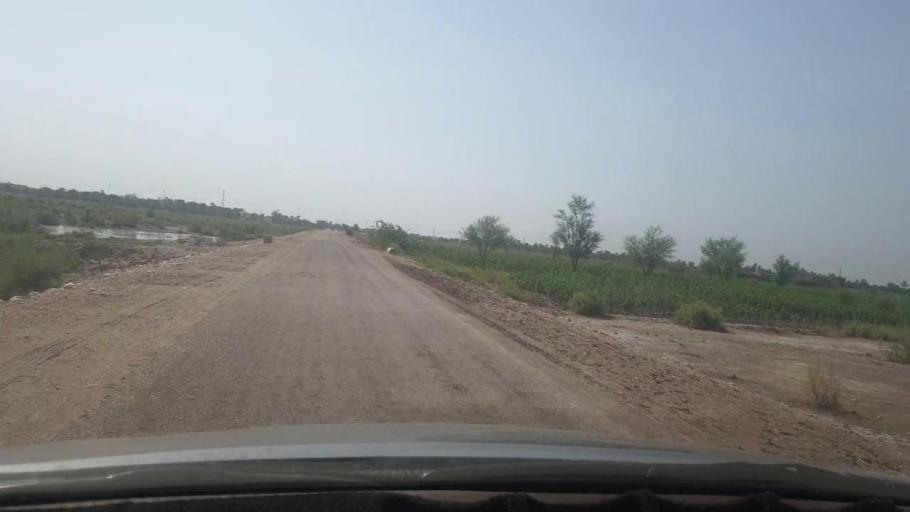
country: PK
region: Sindh
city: Ranipur
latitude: 27.2622
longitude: 68.5841
